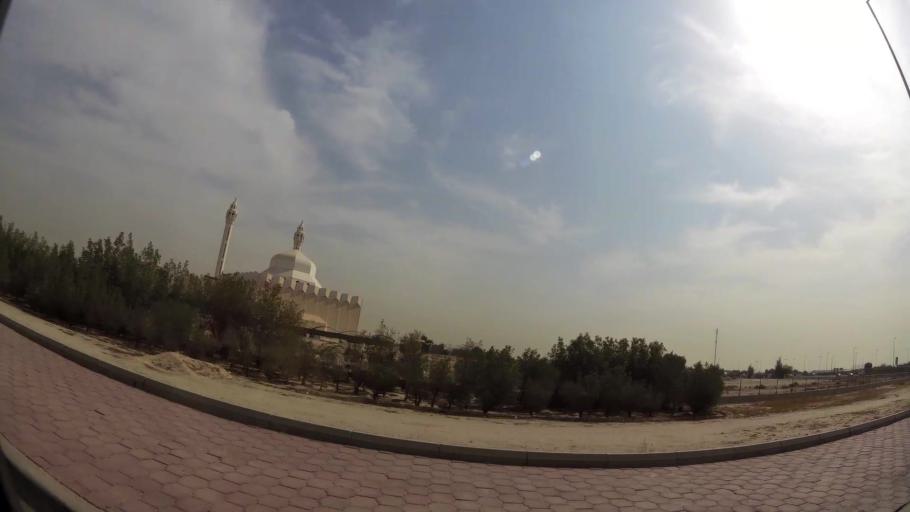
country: KW
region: Al Farwaniyah
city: Janub as Surrah
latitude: 29.2680
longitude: 47.9709
